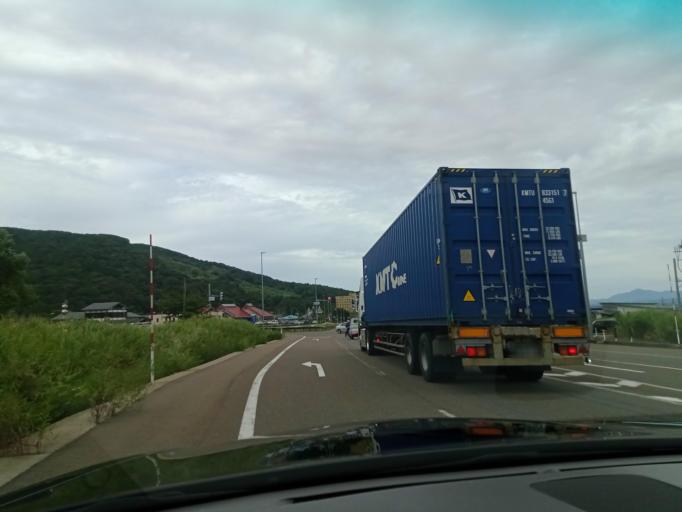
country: JP
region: Niigata
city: Arai
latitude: 37.0238
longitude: 138.2270
